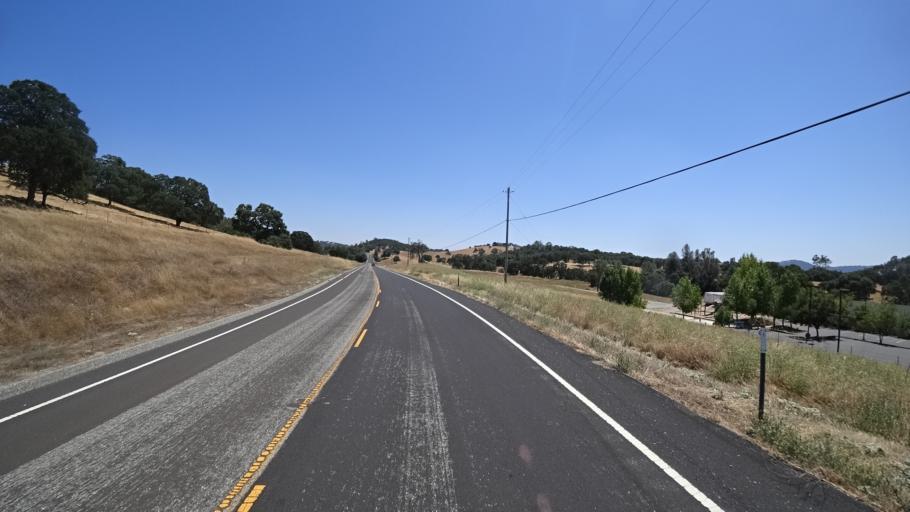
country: US
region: California
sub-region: Calaveras County
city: Angels Camp
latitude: 38.0390
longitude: -120.5326
